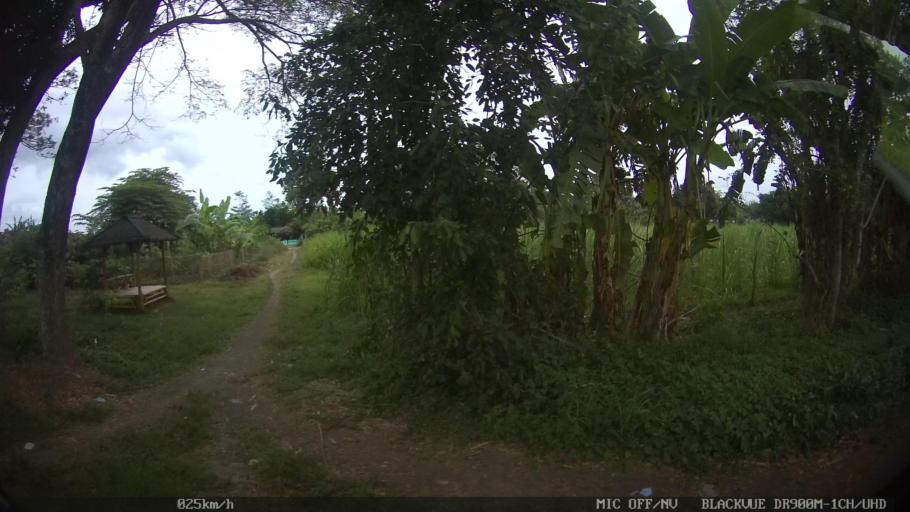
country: ID
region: Daerah Istimewa Yogyakarta
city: Sewon
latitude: -7.8593
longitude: 110.3997
